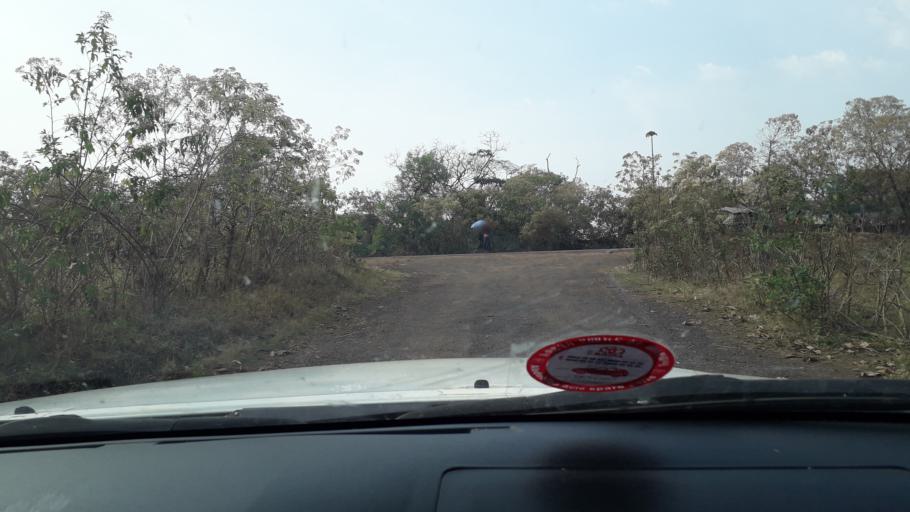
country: ET
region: Southern Nations, Nationalities, and People's Region
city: Mizan Teferi
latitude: 6.8268
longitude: 35.2882
